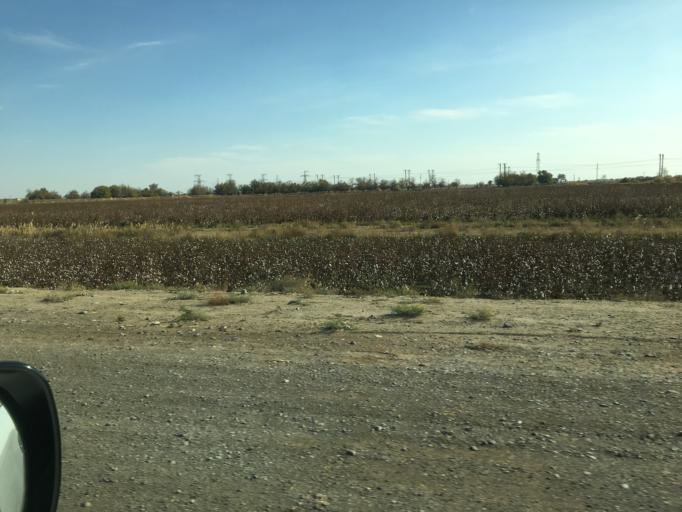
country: TM
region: Mary
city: Mary
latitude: 37.6022
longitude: 61.6726
